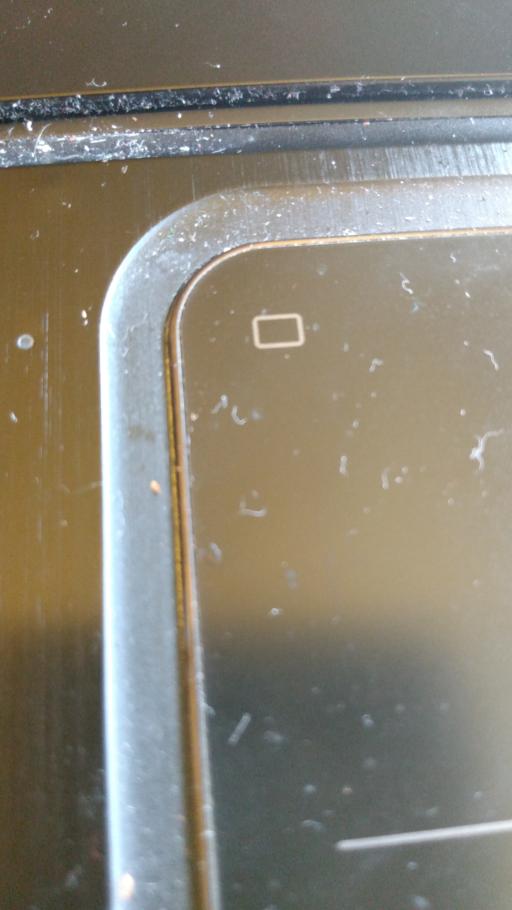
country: RU
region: Moskovskaya
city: Kolomna
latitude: 55.0488
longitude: 38.9019
